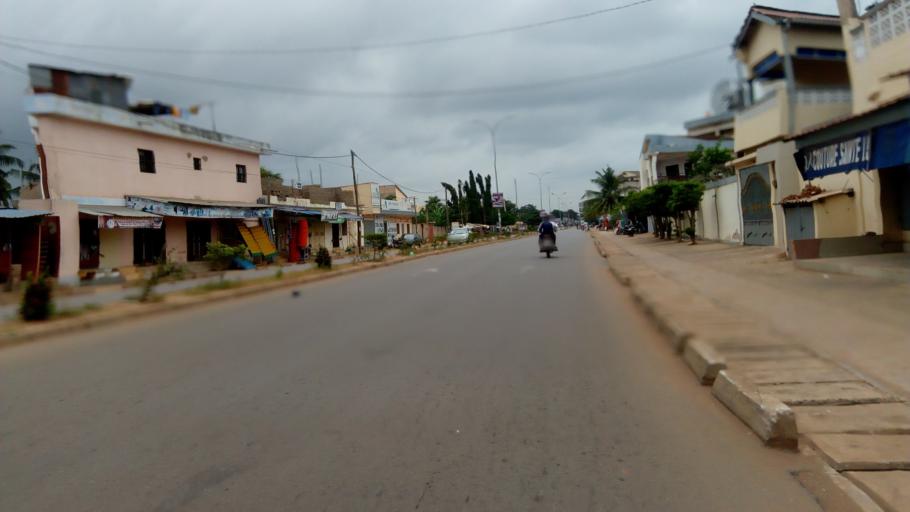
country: TG
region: Maritime
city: Lome
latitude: 6.2183
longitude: 1.2038
